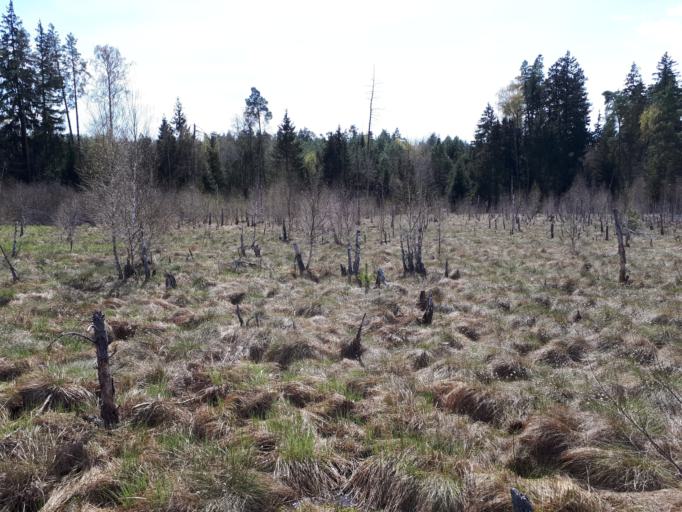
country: LT
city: Ramuciai
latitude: 54.8481
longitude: 24.0779
